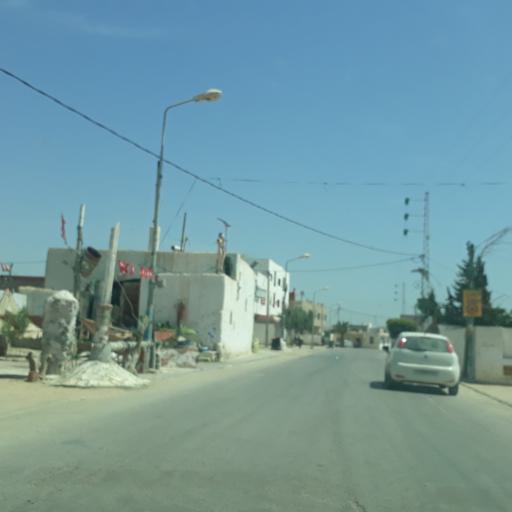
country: TN
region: Safaqis
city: Al Qarmadah
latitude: 34.8168
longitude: 10.7740
